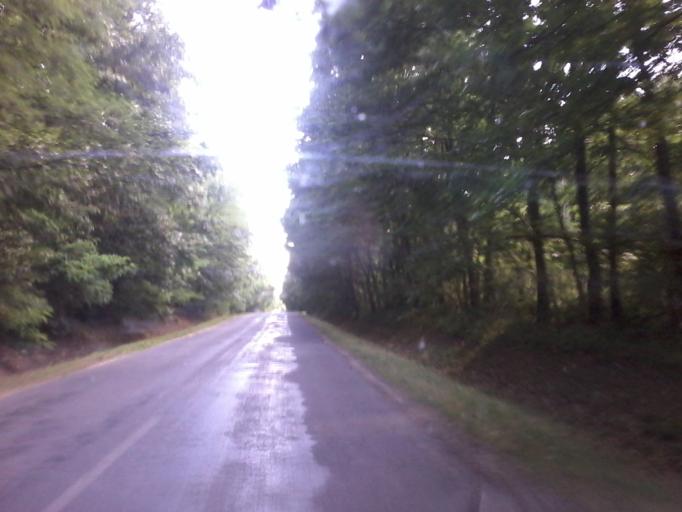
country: HU
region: Vas
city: Janoshaza
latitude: 47.0694
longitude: 17.1205
